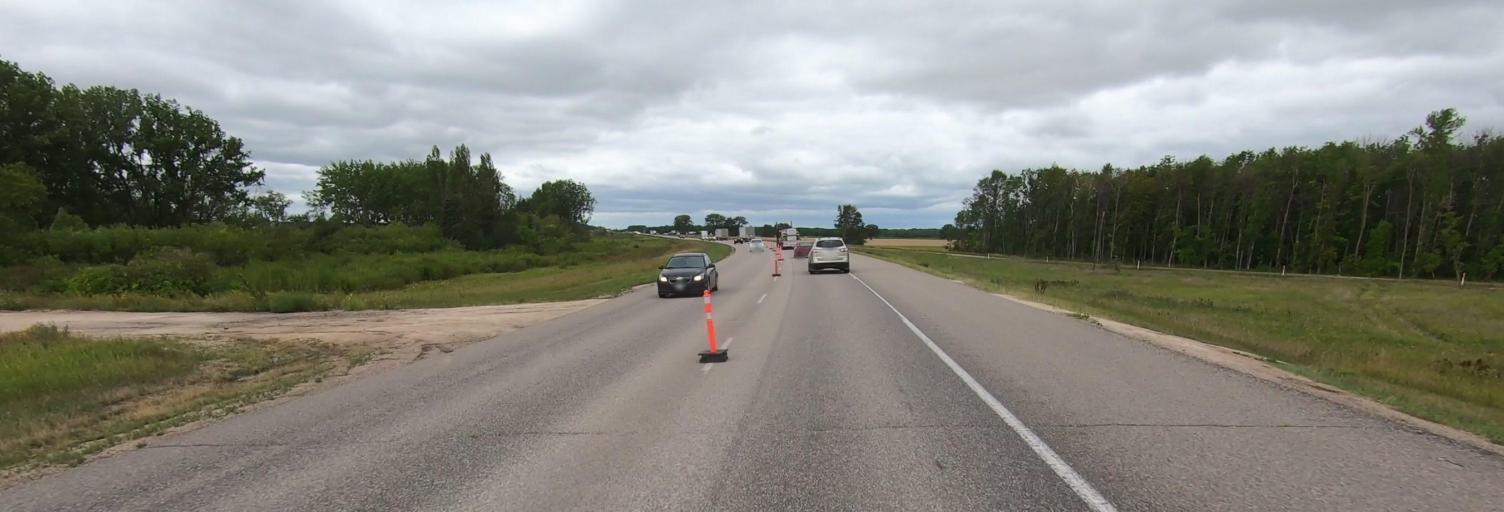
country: CA
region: Manitoba
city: Portage la Prairie
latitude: 49.9722
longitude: -98.1018
